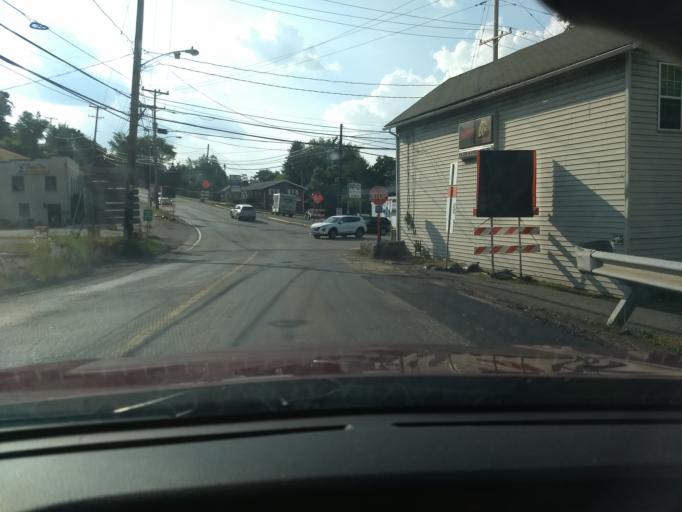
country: US
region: Pennsylvania
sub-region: Allegheny County
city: Plum
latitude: 40.4762
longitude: -79.7600
